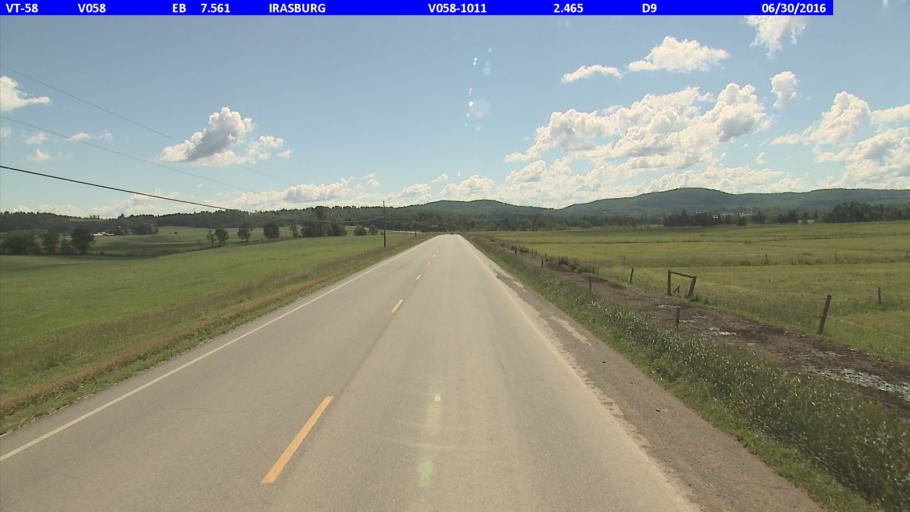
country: US
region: Vermont
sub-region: Orleans County
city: Newport
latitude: 44.8148
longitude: -72.3107
